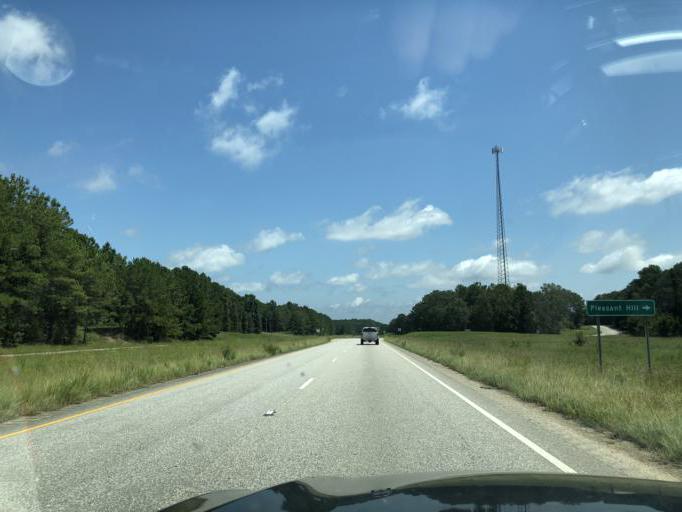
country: US
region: Alabama
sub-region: Henry County
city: Abbeville
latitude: 31.7407
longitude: -85.2461
